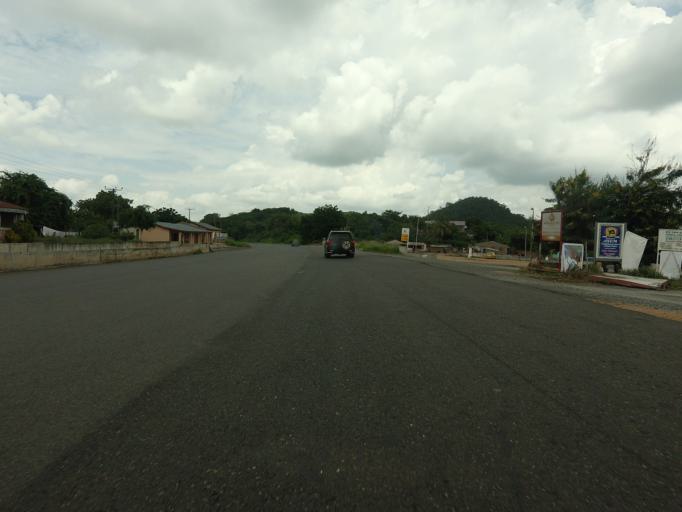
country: GH
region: Volta
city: Ho
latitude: 6.4287
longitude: 0.1683
